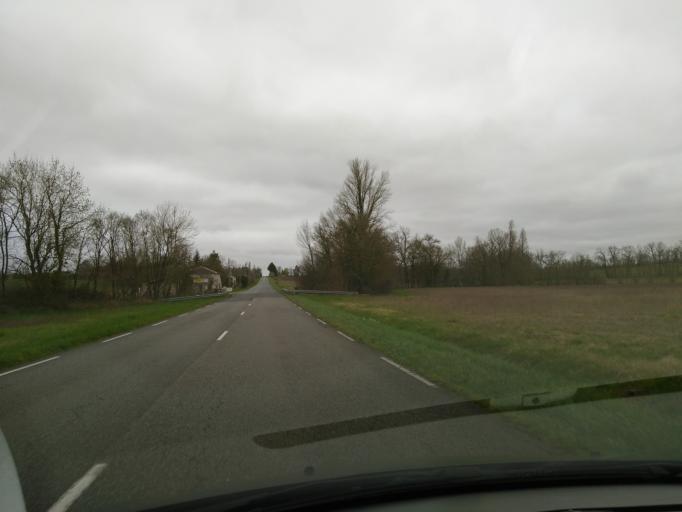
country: FR
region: Aquitaine
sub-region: Departement du Lot-et-Garonne
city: Castillonnes
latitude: 44.6825
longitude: 0.5744
